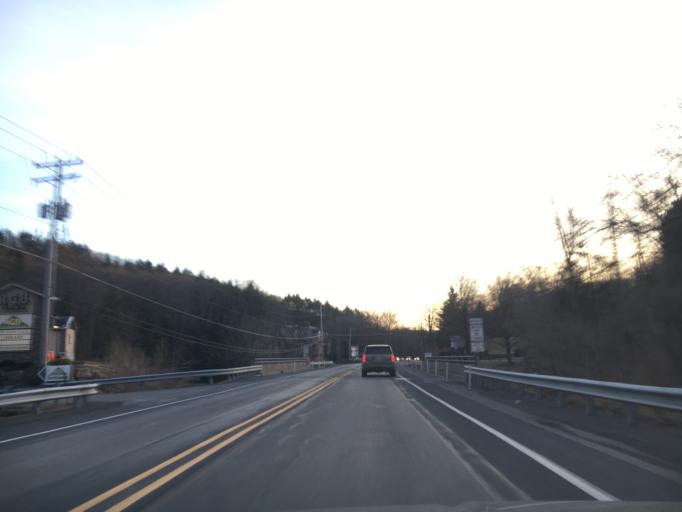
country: US
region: Pennsylvania
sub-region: Monroe County
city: East Stroudsburg
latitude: 41.0162
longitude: -75.1299
